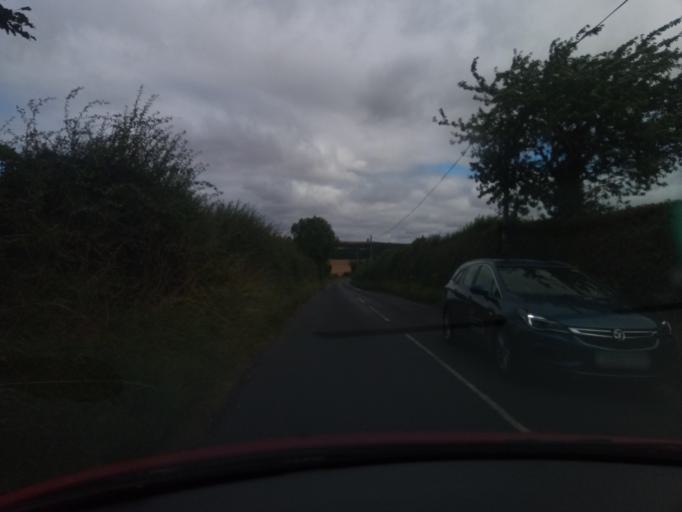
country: GB
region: Scotland
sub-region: The Scottish Borders
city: Kelso
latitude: 55.5293
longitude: -2.4615
